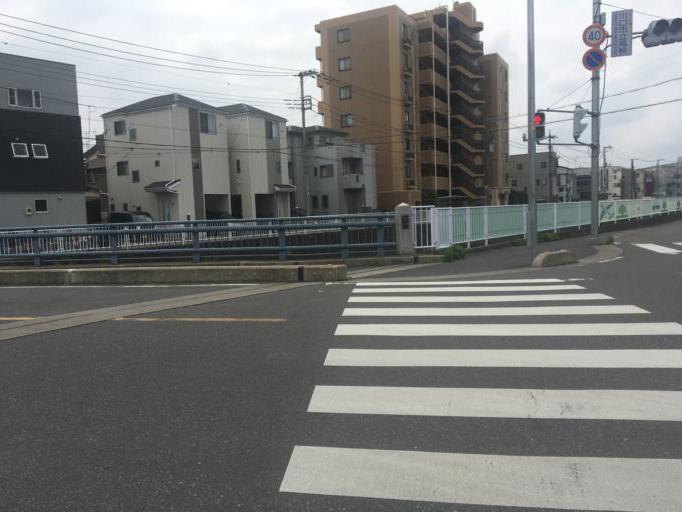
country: JP
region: Saitama
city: Kawaguchi
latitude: 35.8248
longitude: 139.7209
